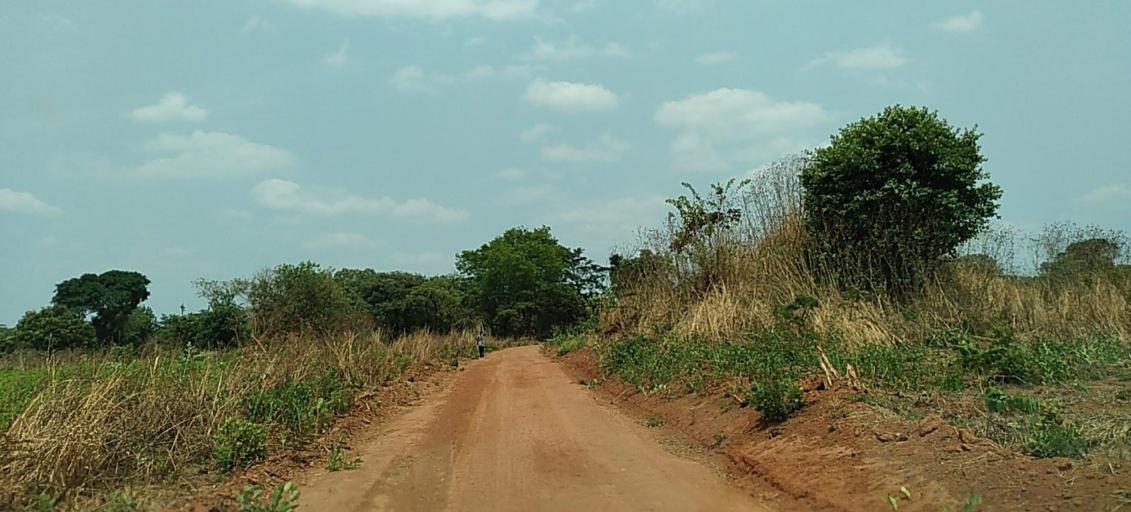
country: ZM
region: Copperbelt
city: Kalulushi
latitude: -12.7588
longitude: 28.0189
